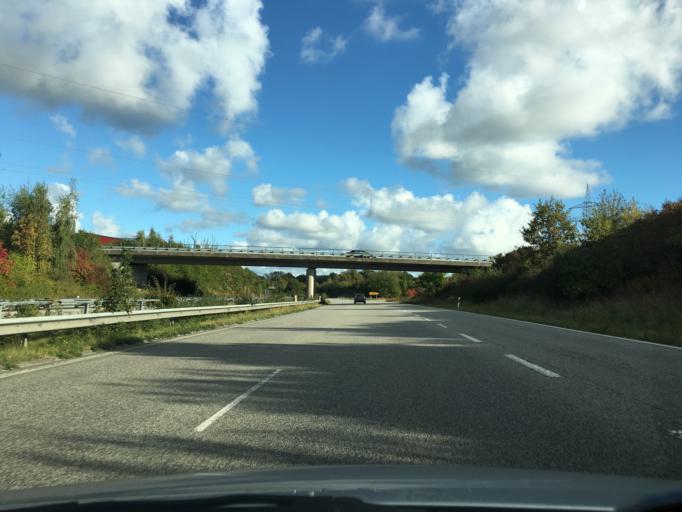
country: DE
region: Schleswig-Holstein
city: Schonkirchen
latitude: 54.3405
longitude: 10.2087
